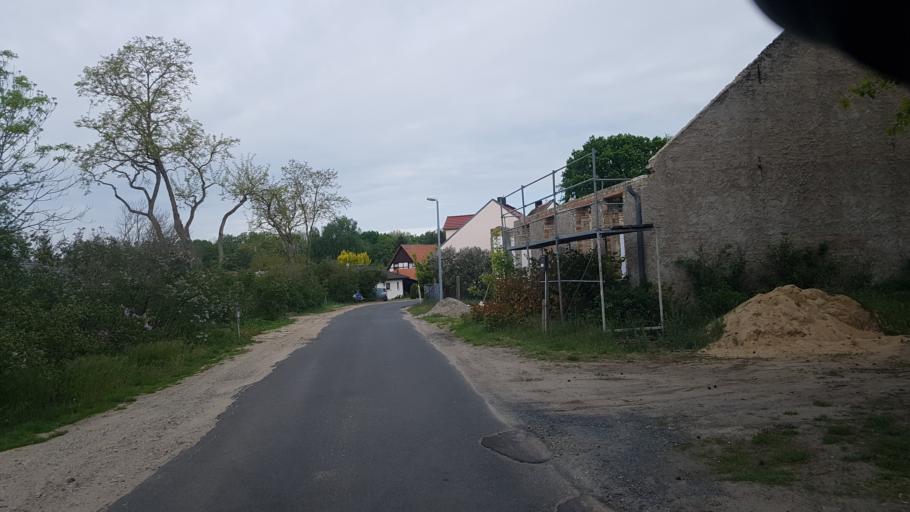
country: DE
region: Brandenburg
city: Luckenwalde
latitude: 52.1274
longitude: 13.0781
